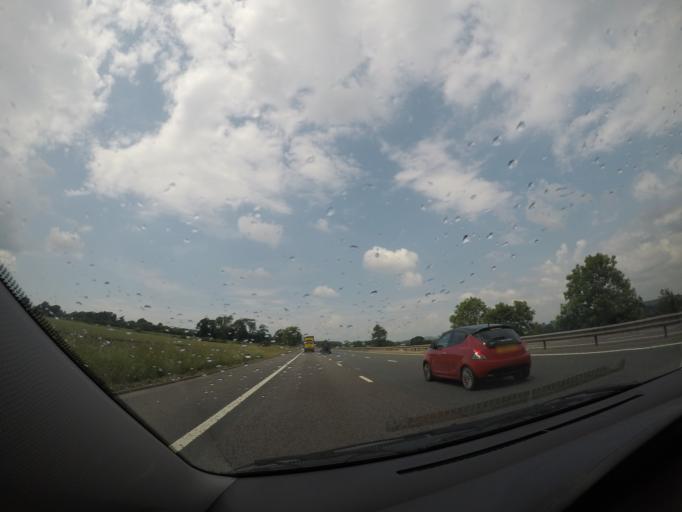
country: GB
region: England
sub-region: Cumbria
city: Penrith
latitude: 54.7516
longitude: -2.8175
